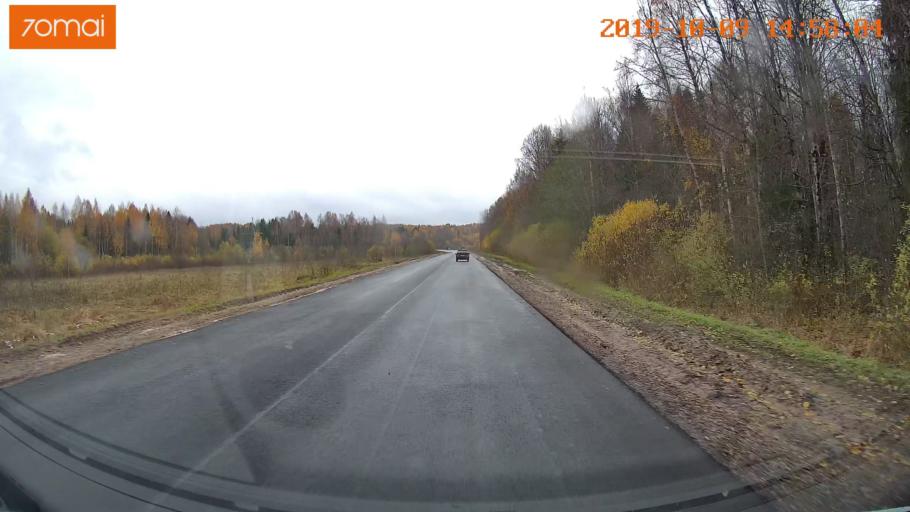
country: RU
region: Kostroma
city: Chistyye Bory
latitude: 58.3308
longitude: 41.6534
